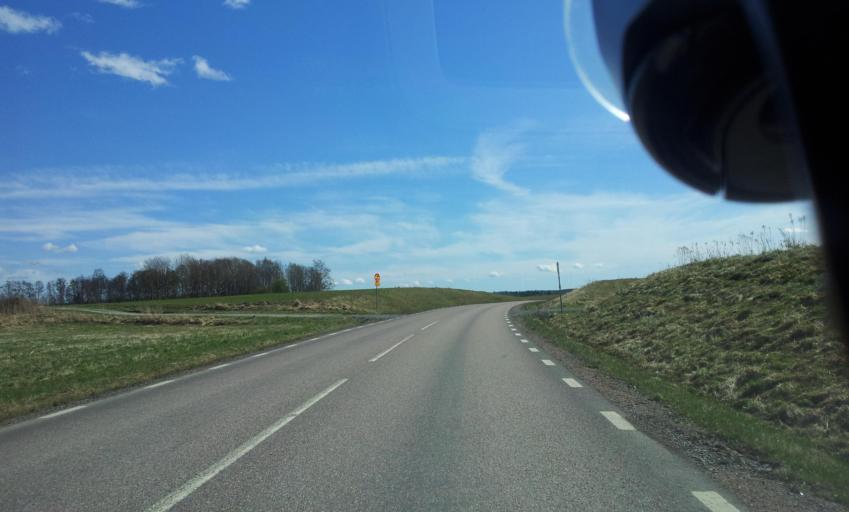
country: SE
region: Dalarna
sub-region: Borlange Kommun
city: Borlaenge
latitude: 60.4831
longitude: 15.4743
